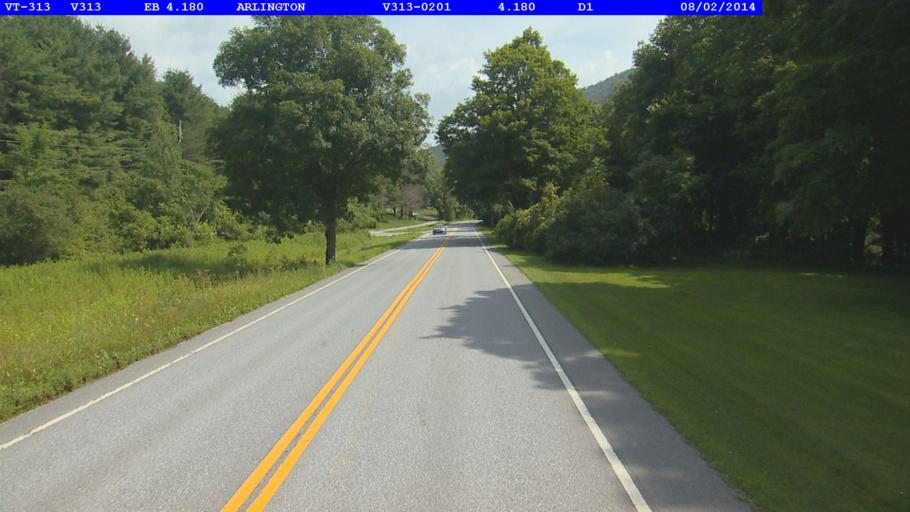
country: US
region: Vermont
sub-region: Bennington County
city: Arlington
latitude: 43.0892
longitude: -73.1947
